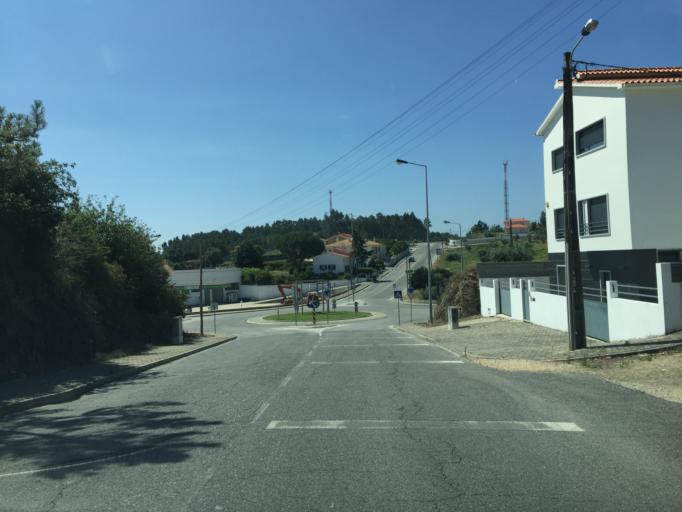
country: PT
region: Castelo Branco
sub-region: Proenca-A-Nova
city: Proenca-a-Nova
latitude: 39.7501
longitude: -7.9179
